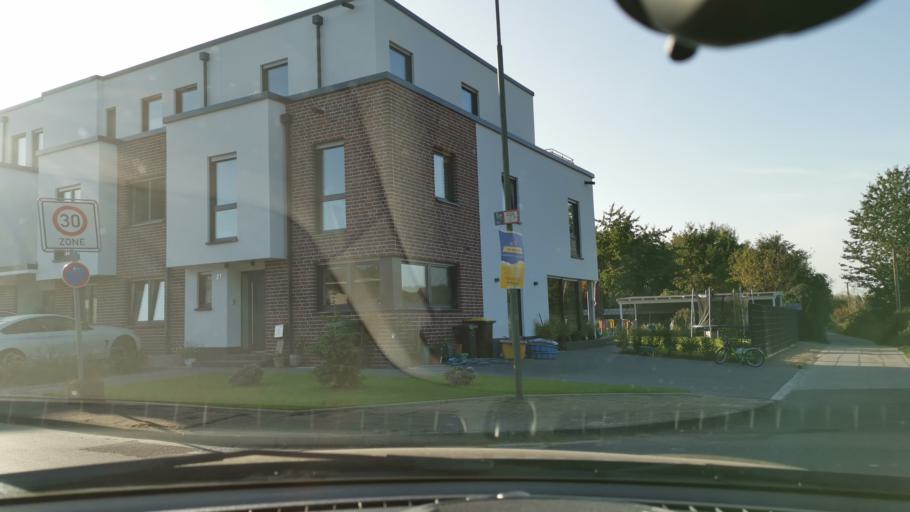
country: DE
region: North Rhine-Westphalia
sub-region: Regierungsbezirk Dusseldorf
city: Dormagen
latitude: 51.1087
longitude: 6.7481
